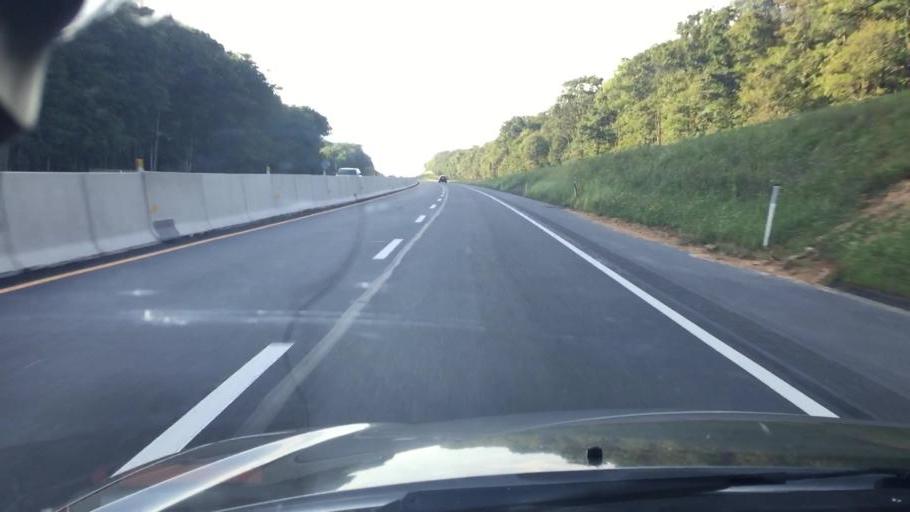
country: US
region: Pennsylvania
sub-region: Carbon County
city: Towamensing Trails
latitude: 41.0244
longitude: -75.6481
